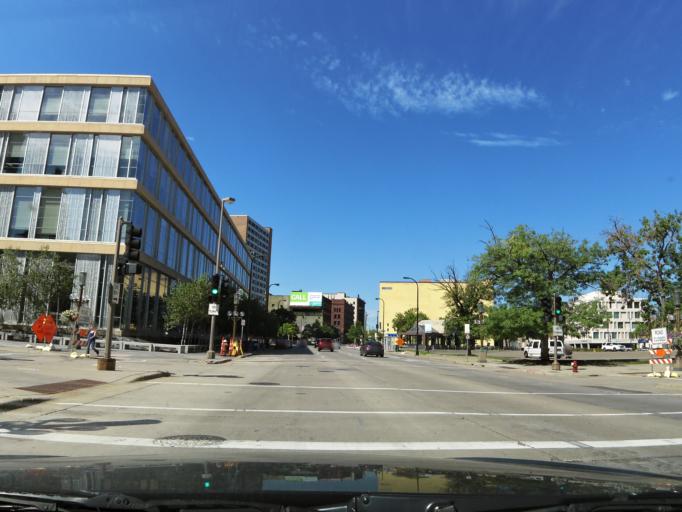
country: US
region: Minnesota
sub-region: Hennepin County
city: Minneapolis
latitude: 44.9807
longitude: -93.2688
